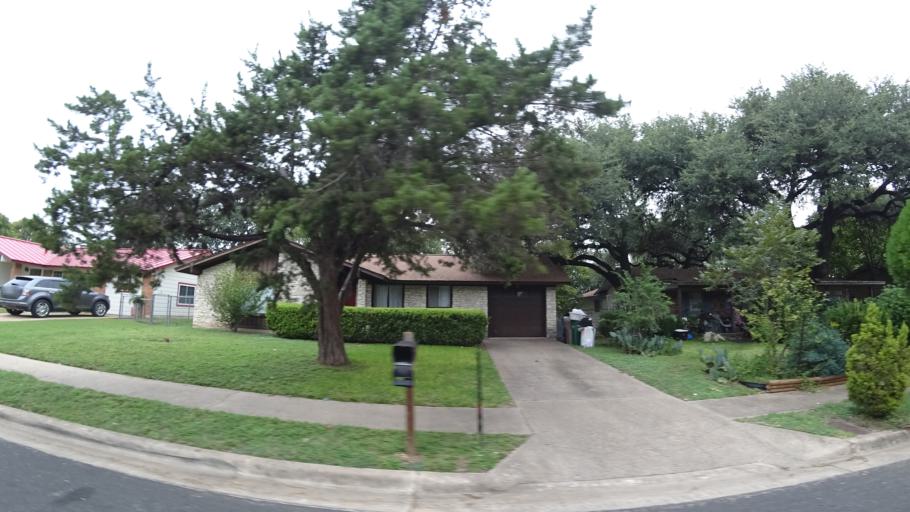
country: US
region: Texas
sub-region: Travis County
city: Onion Creek
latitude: 30.2033
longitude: -97.7792
